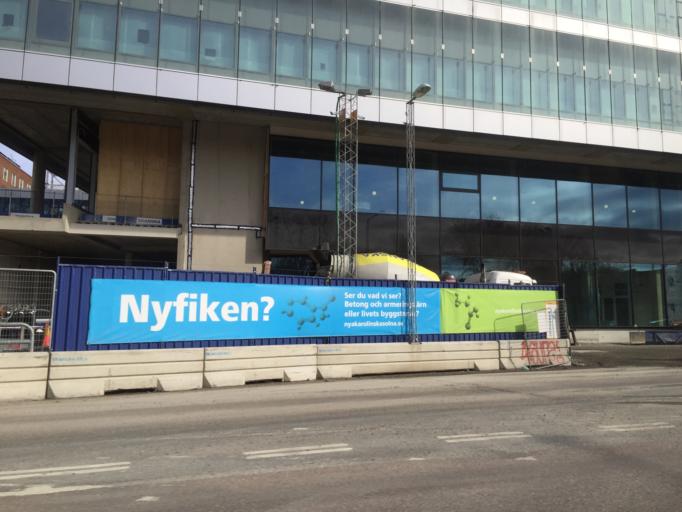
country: SE
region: Stockholm
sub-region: Solna Kommun
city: Solna
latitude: 59.3486
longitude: 18.0286
